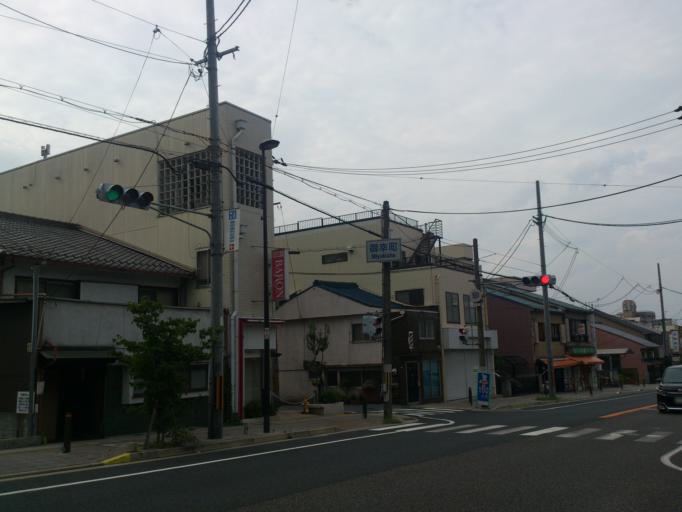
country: JP
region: Shiga Prefecture
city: Otsu-shi
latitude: 35.0051
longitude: 135.8612
